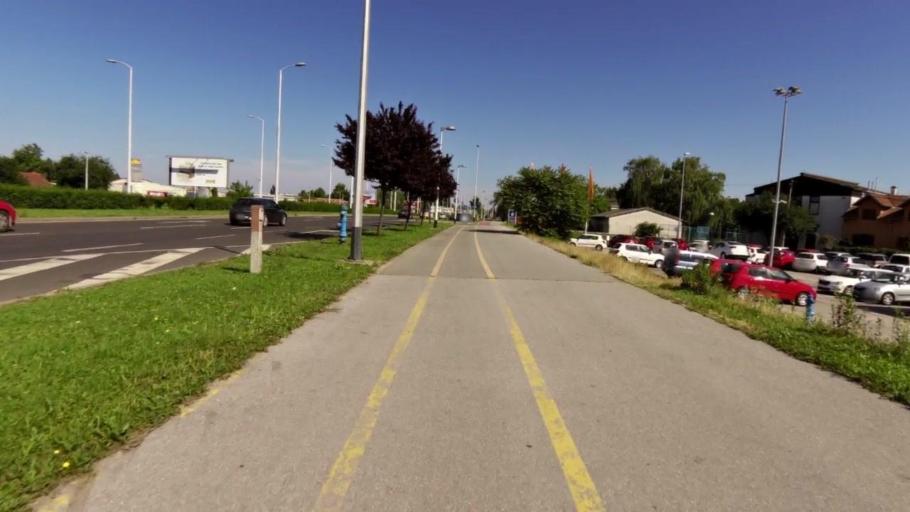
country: HR
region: Grad Zagreb
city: Novi Zagreb
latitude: 45.7960
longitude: 16.0191
